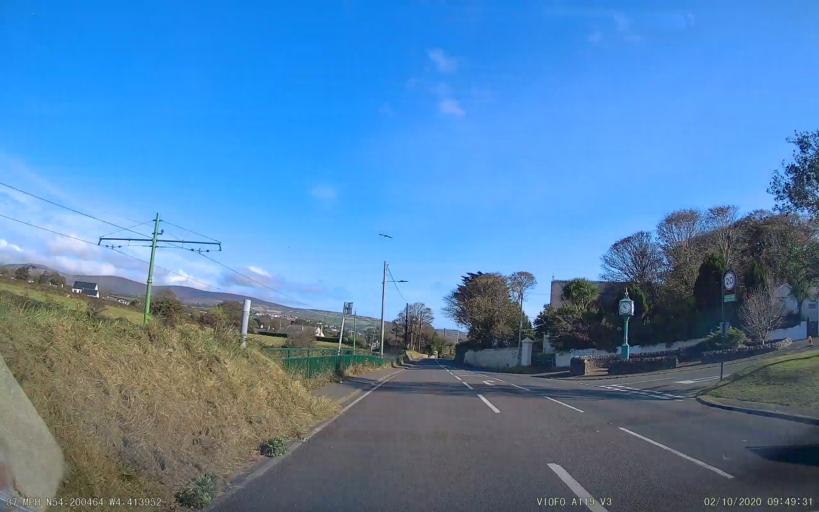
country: IM
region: Laxey
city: Laxey
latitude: 54.2005
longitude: -4.4140
